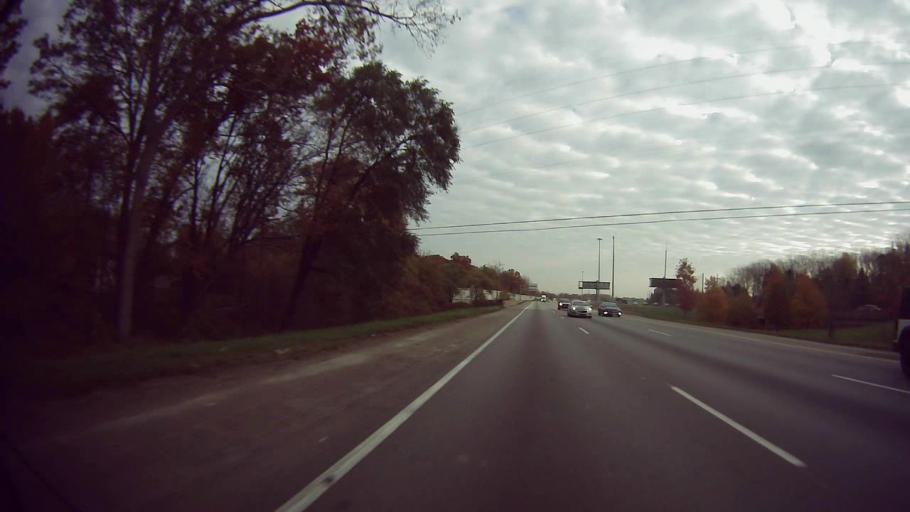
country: US
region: Michigan
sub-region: Wayne County
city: Taylor
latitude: 42.2613
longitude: -83.2903
